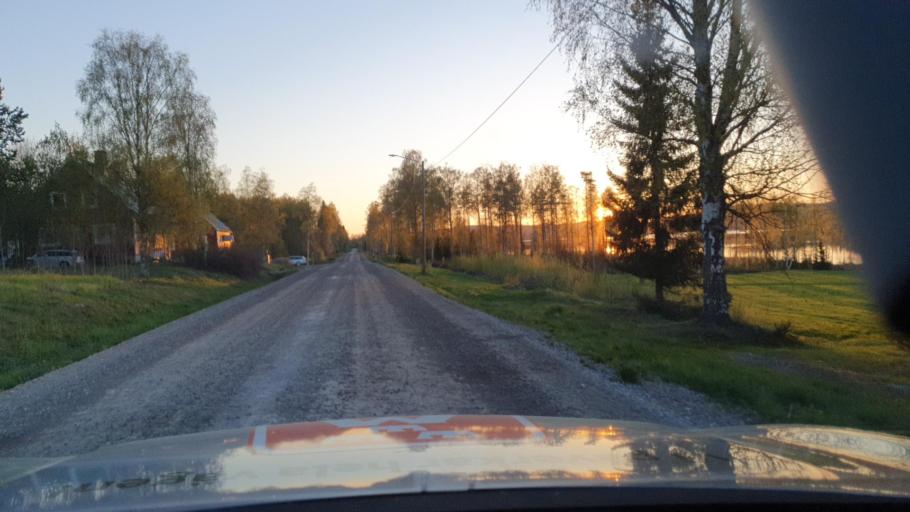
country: SE
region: Vaesternorrland
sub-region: OErnskoeldsviks Kommun
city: Bjasta
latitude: 63.5030
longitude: 18.4864
